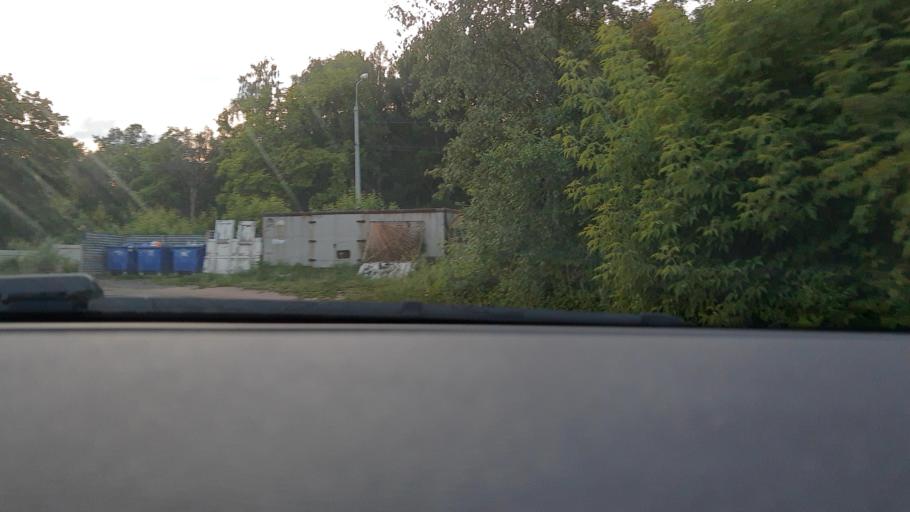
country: RU
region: Nizjnij Novgorod
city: Kstovo
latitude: 56.1567
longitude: 44.2556
